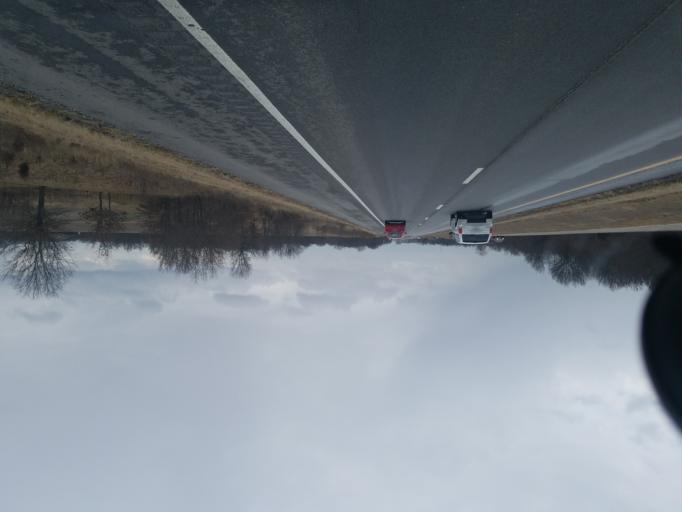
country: US
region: Missouri
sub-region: Randolph County
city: Moberly
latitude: 39.3744
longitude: -92.4118
